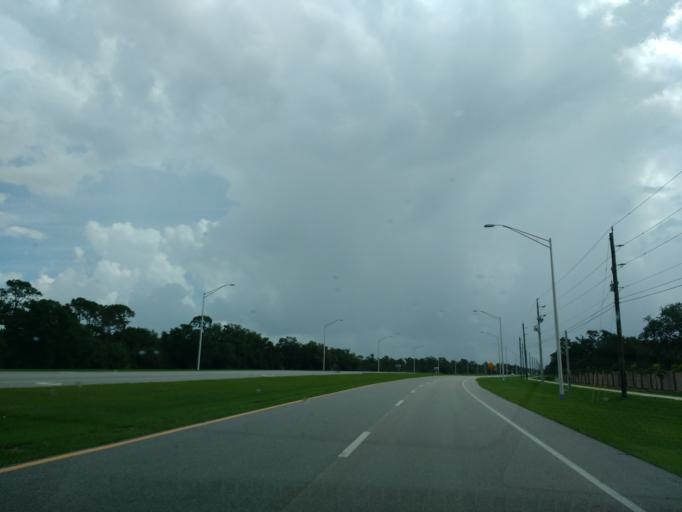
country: US
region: Florida
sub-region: Lee County
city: Burnt Store Marina
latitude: 26.8013
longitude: -82.0358
